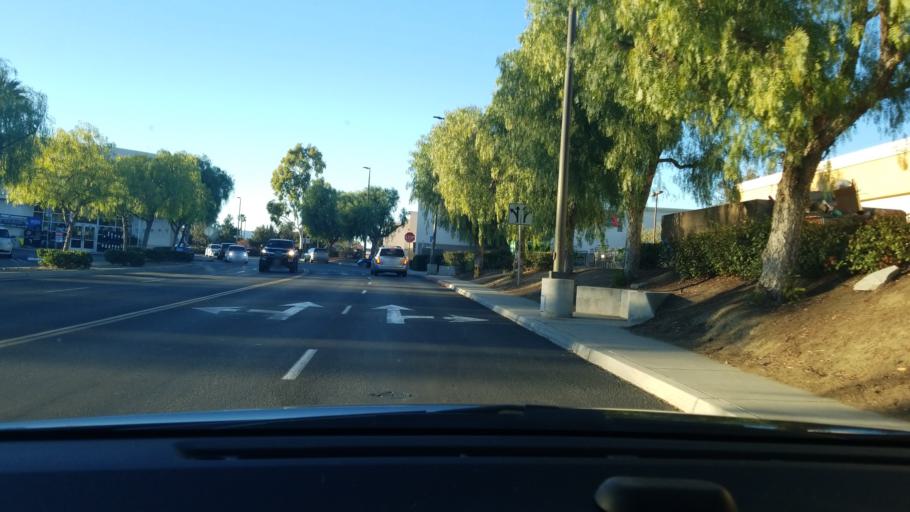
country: US
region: California
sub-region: Riverside County
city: Murrieta Hot Springs
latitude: 33.5274
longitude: -117.1522
